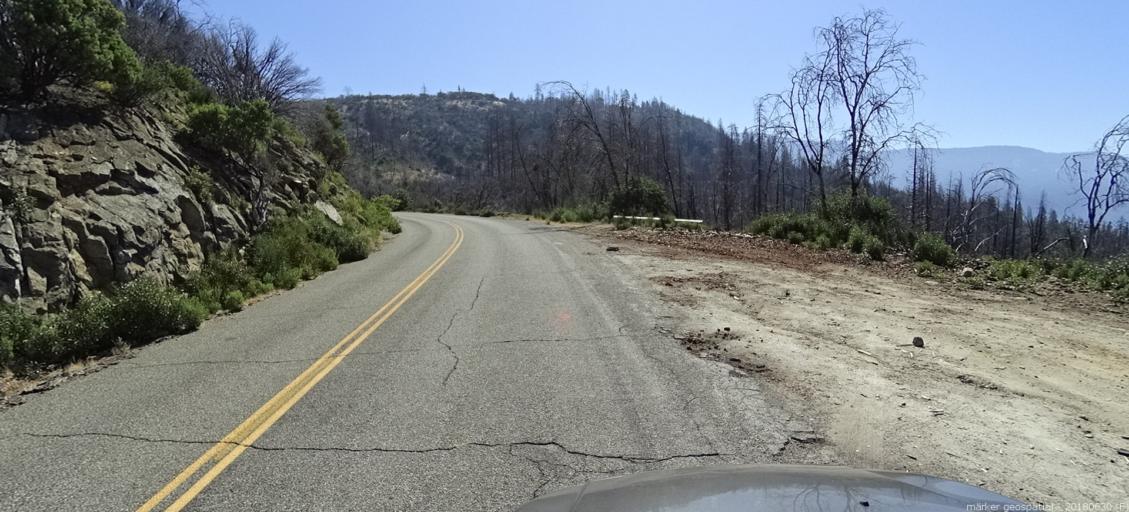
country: US
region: California
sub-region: Fresno County
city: Auberry
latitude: 37.2990
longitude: -119.3614
